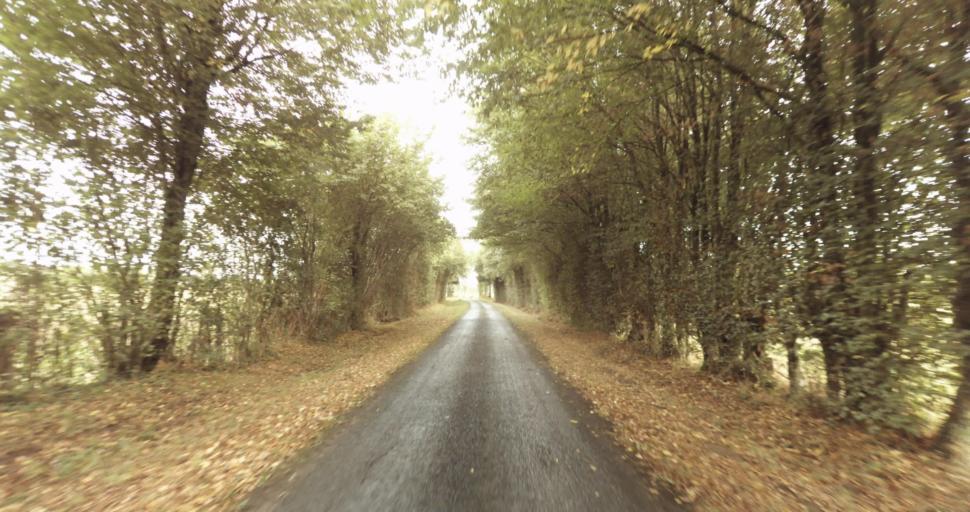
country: FR
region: Lower Normandy
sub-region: Departement de l'Orne
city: Sainte-Gauburge-Sainte-Colombe
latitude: 48.6931
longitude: 0.3517
